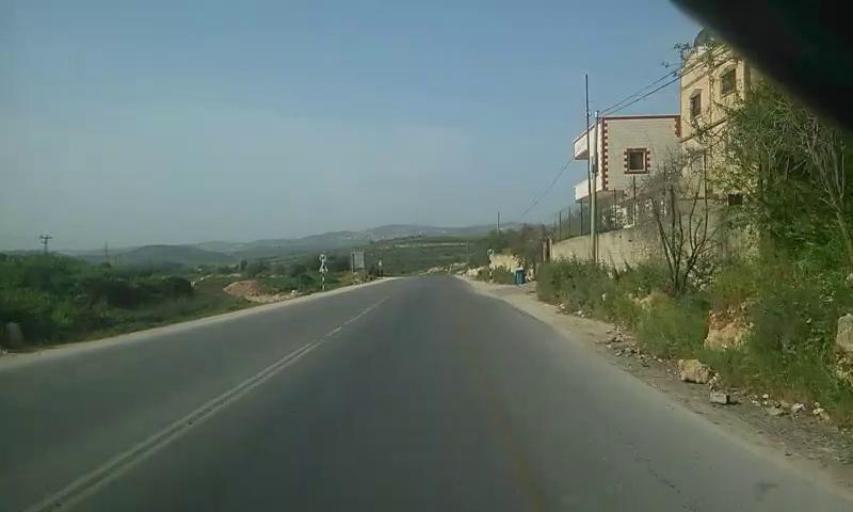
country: PS
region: West Bank
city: Dayr Sharaf
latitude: 32.2541
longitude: 35.1776
